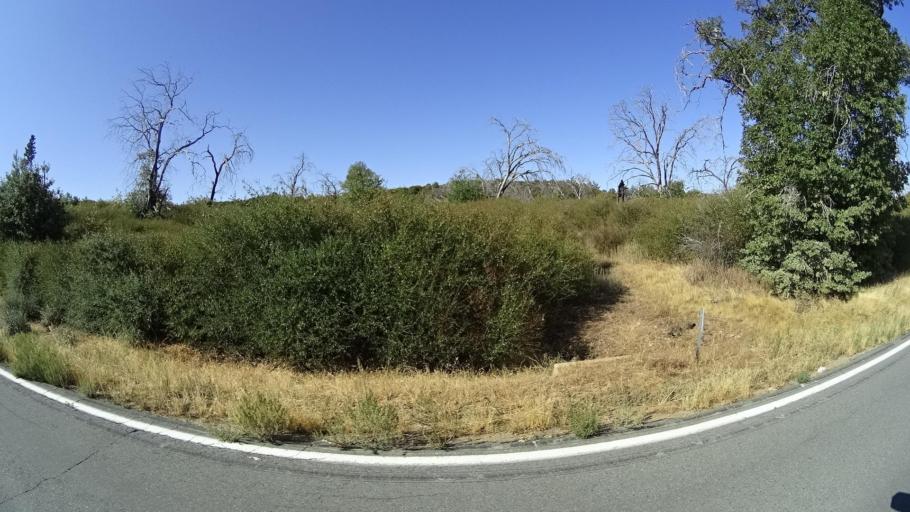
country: US
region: California
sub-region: San Diego County
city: Pine Valley
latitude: 32.9045
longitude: -116.4566
